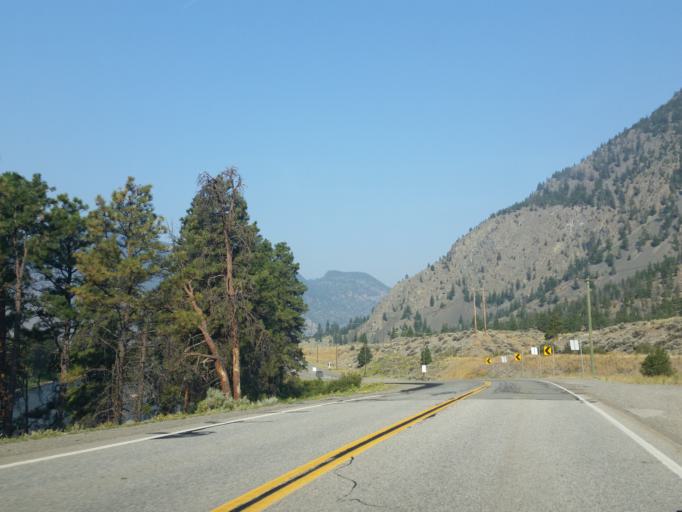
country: CA
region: British Columbia
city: Oliver
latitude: 49.2198
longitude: -119.9334
